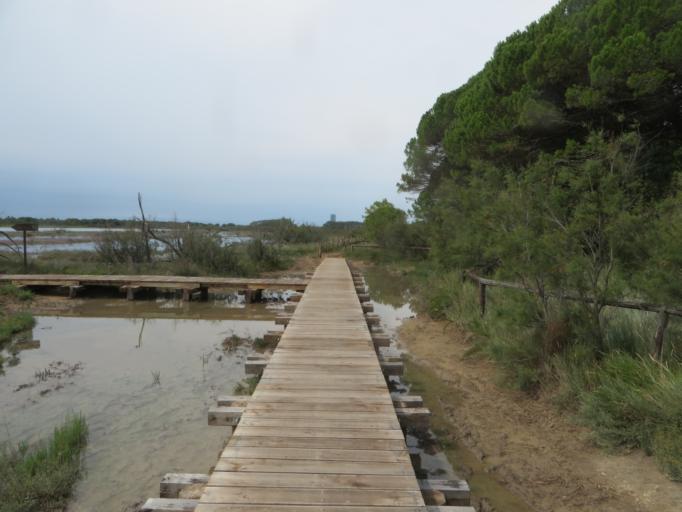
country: IT
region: Veneto
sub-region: Provincia di Venezia
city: Crepaldo
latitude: 45.5391
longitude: 12.7424
